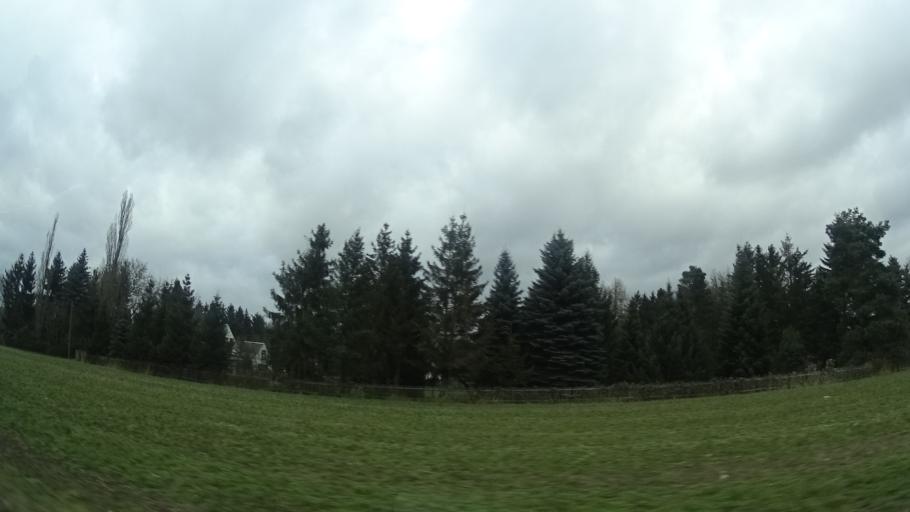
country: DE
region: Thuringia
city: Zeulenroda
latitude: 50.6327
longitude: 11.9914
